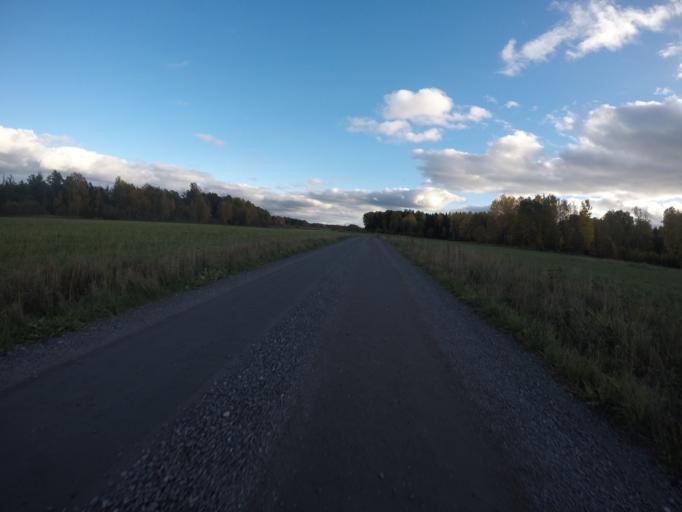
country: SE
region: Vaestmanland
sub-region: Arboga Kommun
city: Tyringe
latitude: 59.3108
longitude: 15.9744
